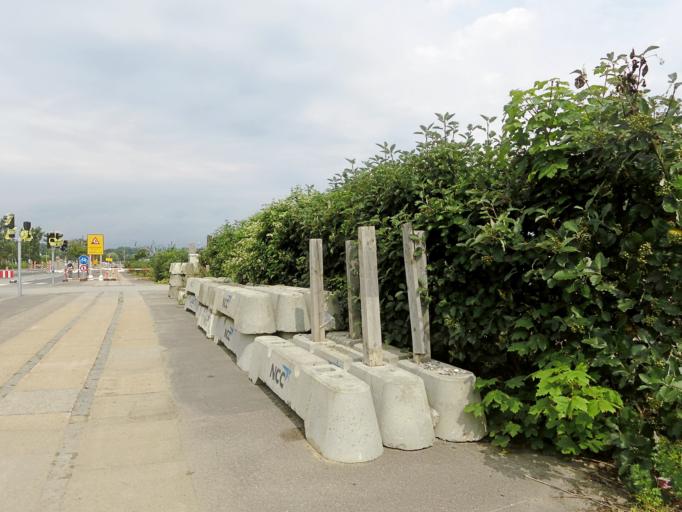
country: DK
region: Capital Region
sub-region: Gentofte Kommune
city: Charlottenlund
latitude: 55.7637
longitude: 12.5989
